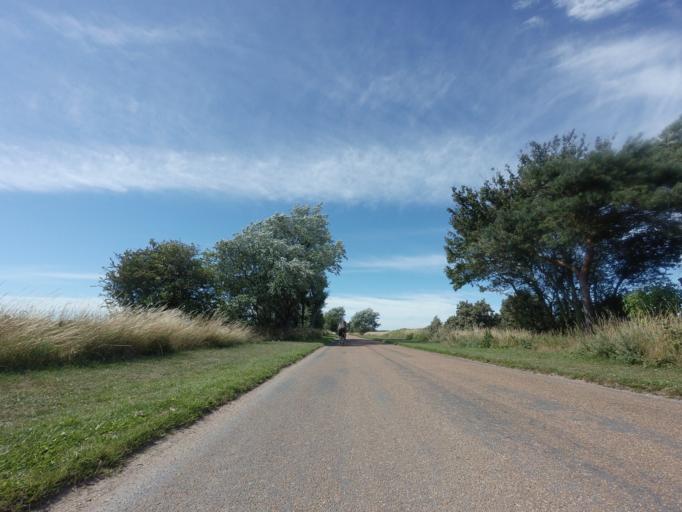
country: GB
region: England
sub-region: Kent
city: Sandwich
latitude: 51.2669
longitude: 1.3784
